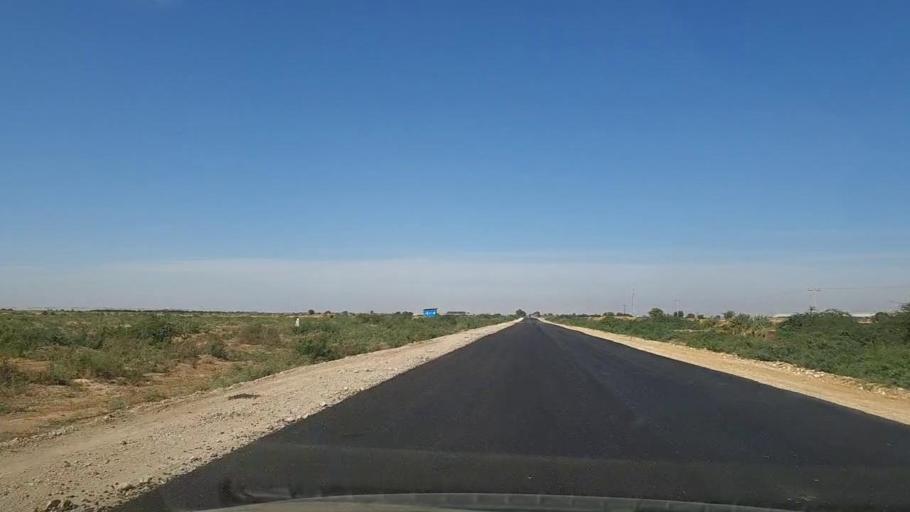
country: PK
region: Sindh
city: Kotri
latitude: 25.2400
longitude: 68.2314
